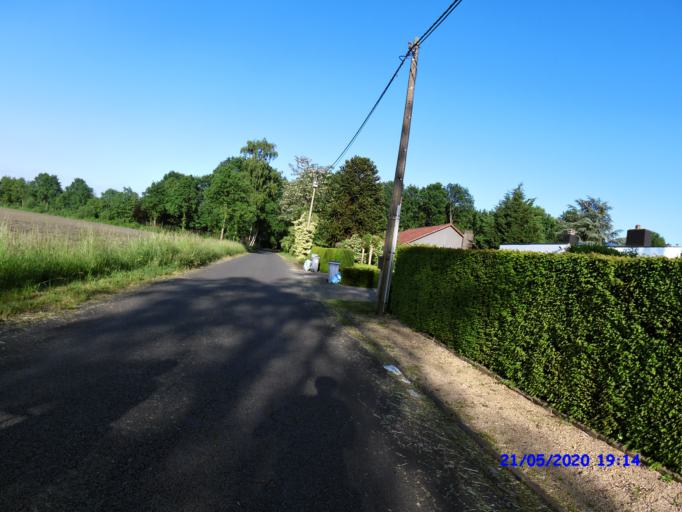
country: BE
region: Flanders
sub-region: Provincie Antwerpen
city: Geel
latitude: 51.1919
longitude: 5.0169
